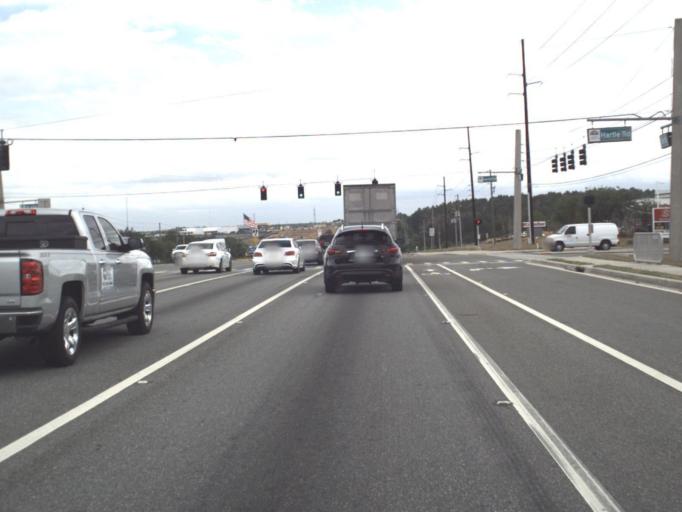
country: US
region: Florida
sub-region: Orange County
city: Oakland
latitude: 28.5464
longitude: -81.6831
